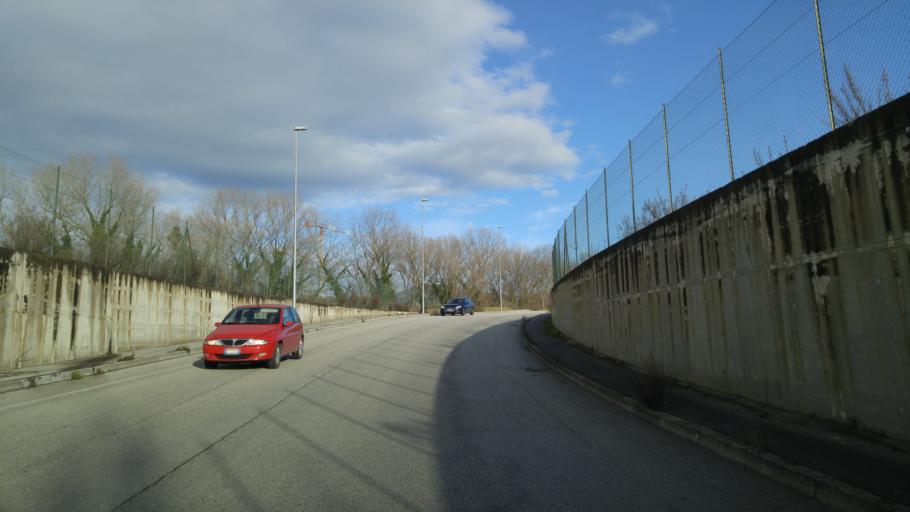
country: IT
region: The Marches
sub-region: Provincia di Ancona
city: San Biagio
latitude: 43.5318
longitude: 13.5206
